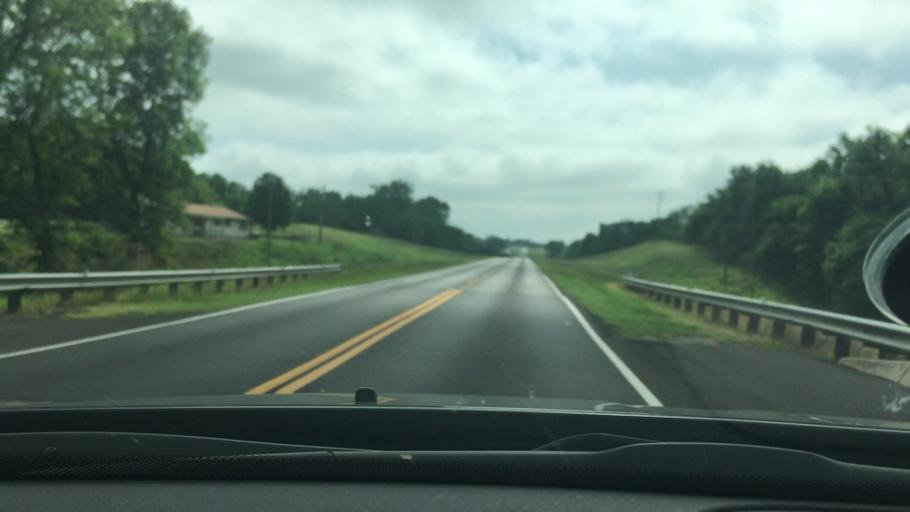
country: US
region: Oklahoma
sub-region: Johnston County
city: Tishomingo
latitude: 34.2303
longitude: -96.6451
